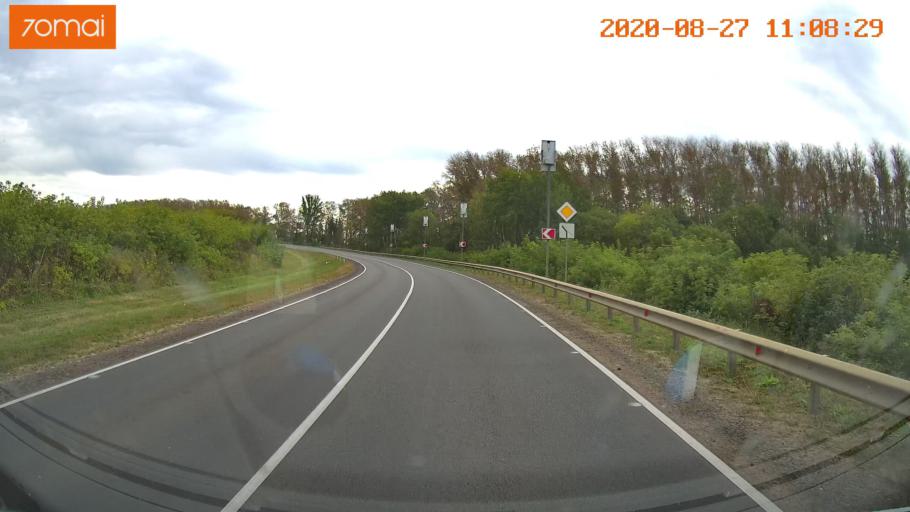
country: RU
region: Rjazan
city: Oktyabr'skiy
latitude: 54.1402
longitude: 38.6910
